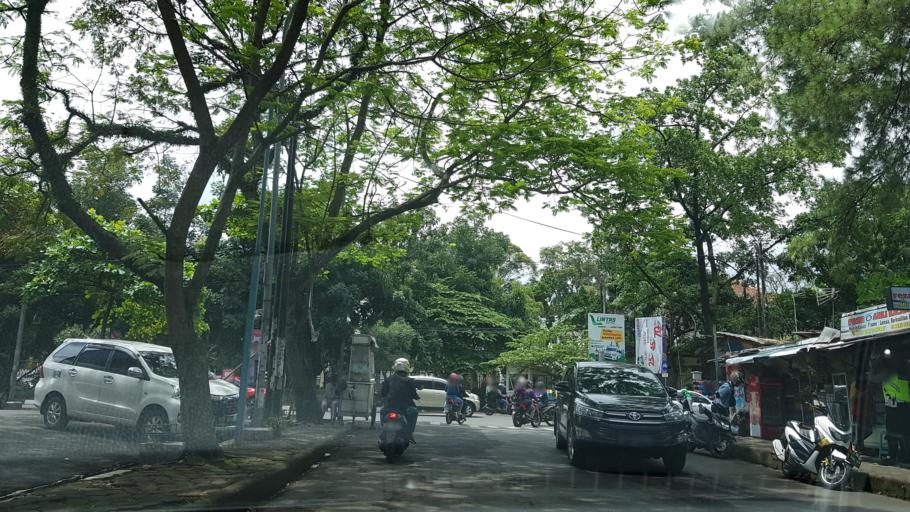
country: ID
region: West Java
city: Bandung
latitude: -6.8958
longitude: 107.6171
